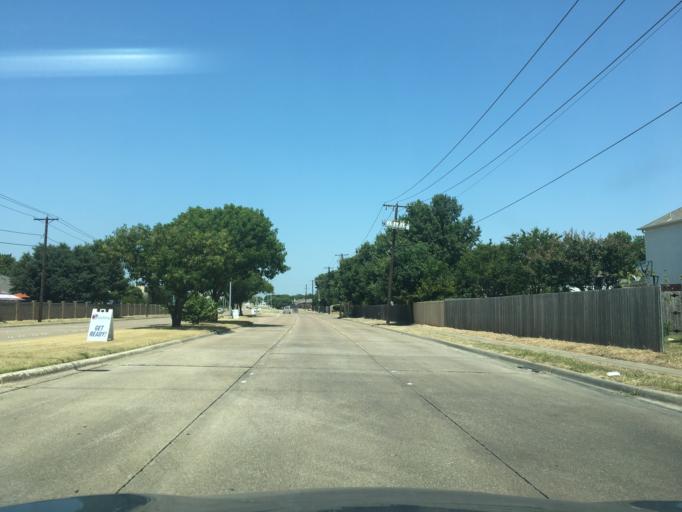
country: US
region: Texas
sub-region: Tarrant County
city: Crowley
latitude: 32.6205
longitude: -97.3699
